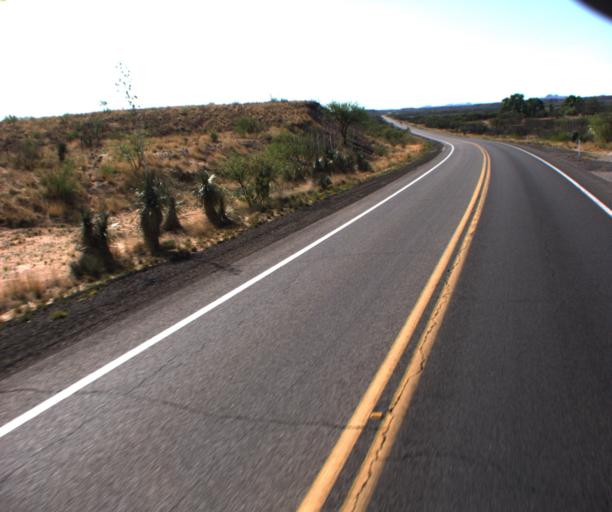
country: US
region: Arizona
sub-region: Cochise County
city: Saint David
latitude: 31.8519
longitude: -110.1998
